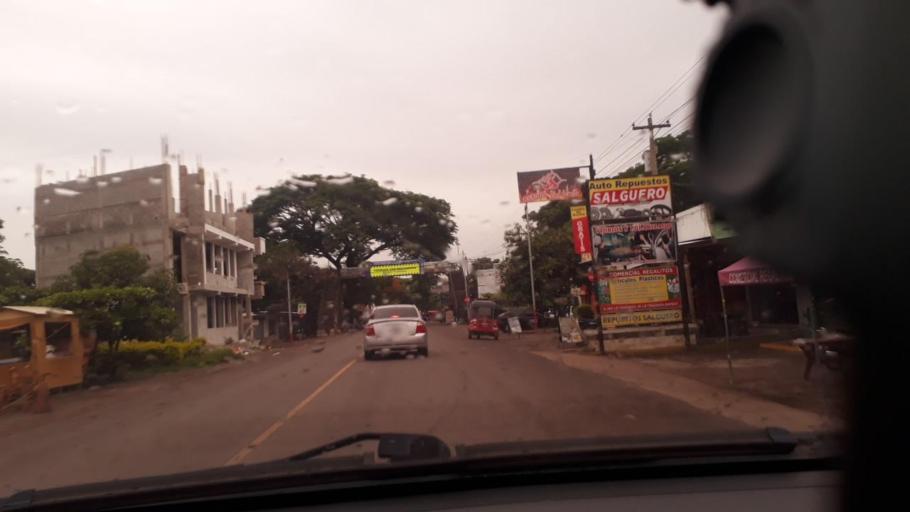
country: GT
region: Jutiapa
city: Asuncion Mita
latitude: 14.3339
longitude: -89.7126
